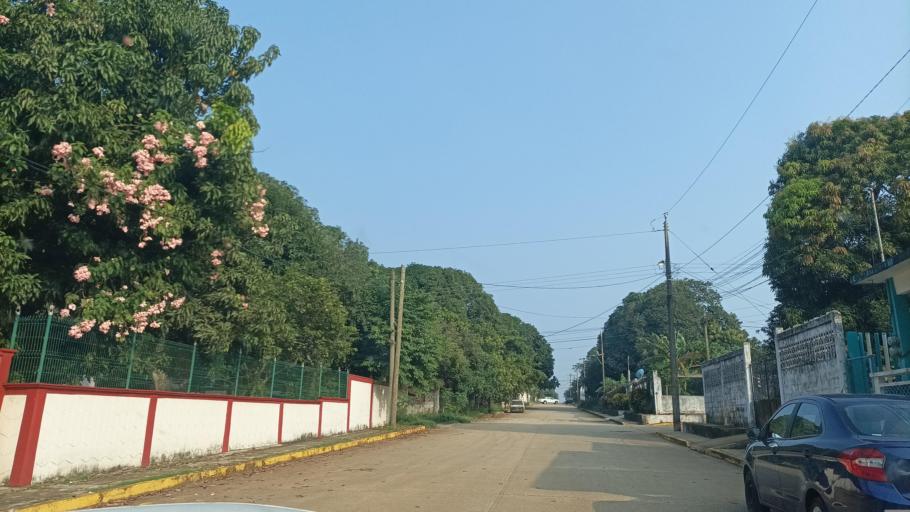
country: MX
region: Veracruz
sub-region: Cosoleacaque
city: Residencial las Olas
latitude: 18.1009
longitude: -94.5722
